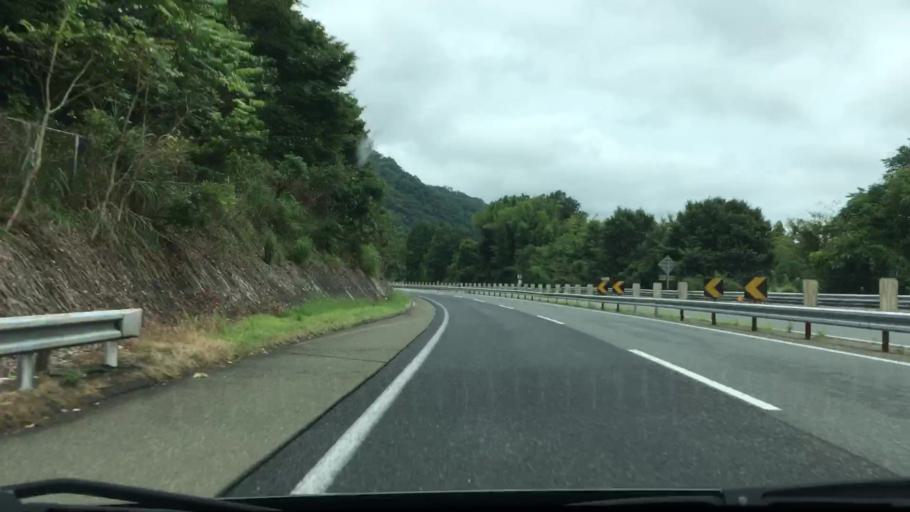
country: JP
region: Hiroshima
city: Shobara
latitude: 34.8407
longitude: 133.0833
